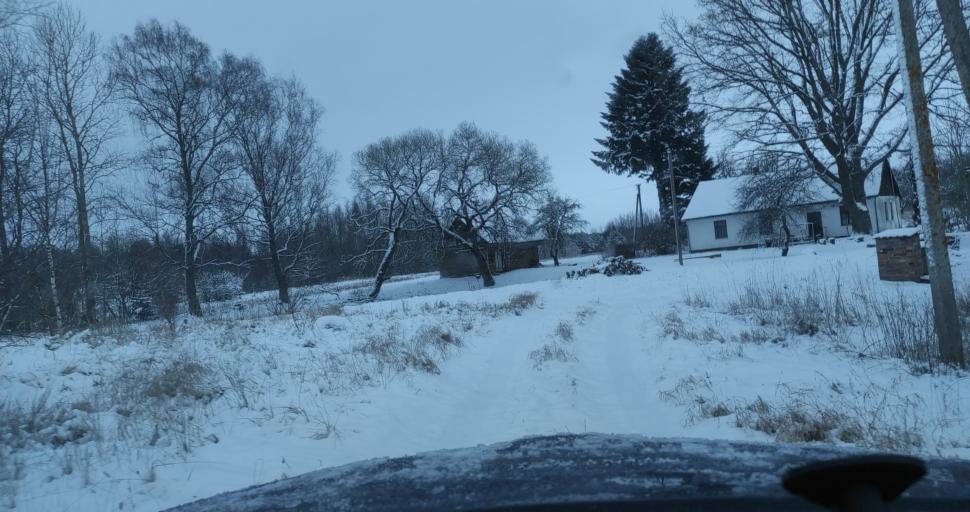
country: LV
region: Alsunga
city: Alsunga
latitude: 56.9569
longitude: 21.6233
